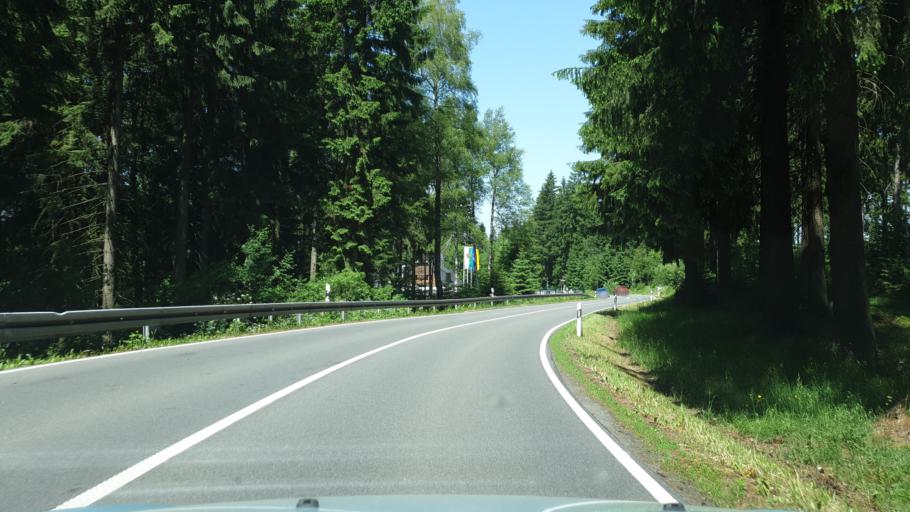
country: DE
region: Saxony
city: Hammerbrucke
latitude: 50.4111
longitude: 12.4078
